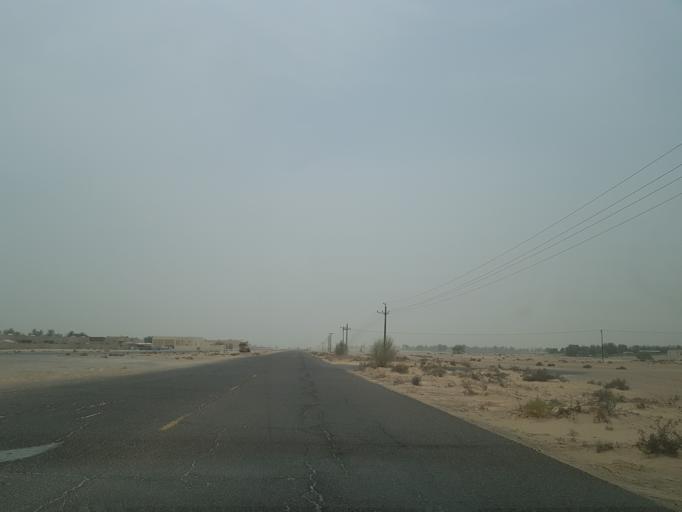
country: AE
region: Dubai
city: Dubai
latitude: 24.9385
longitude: 55.4758
